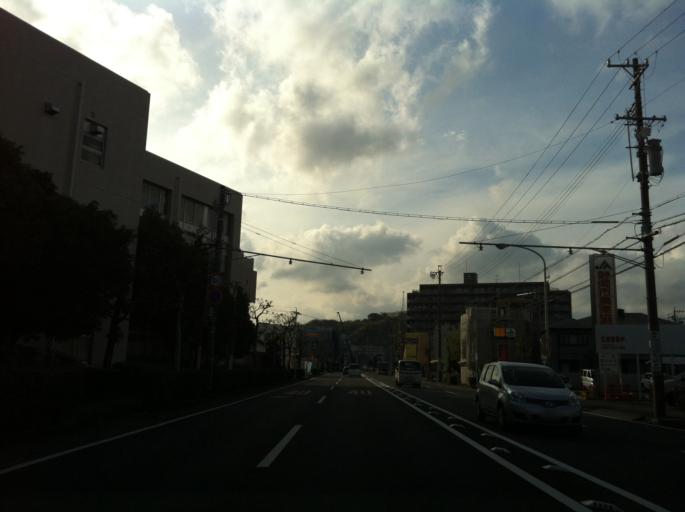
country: JP
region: Shizuoka
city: Shizuoka-shi
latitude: 34.9770
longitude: 138.4122
